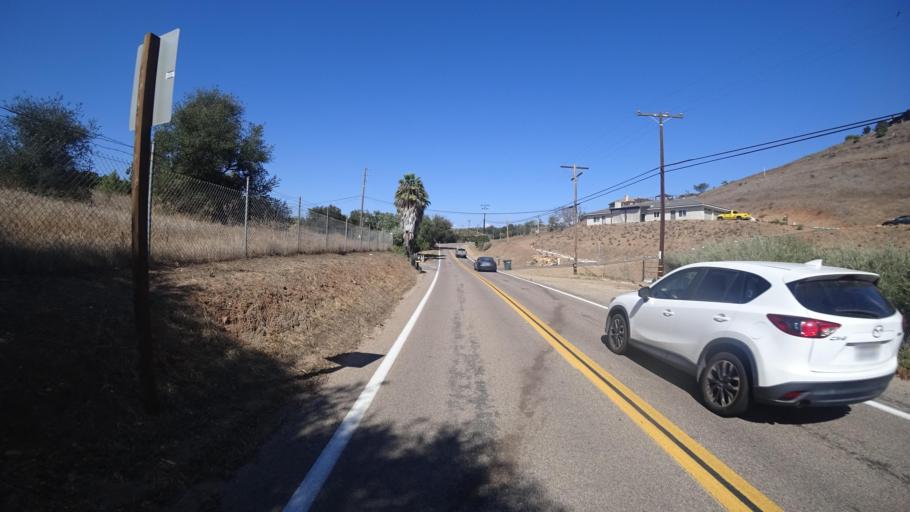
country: US
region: California
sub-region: San Diego County
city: Hidden Meadows
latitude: 33.2659
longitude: -117.1300
